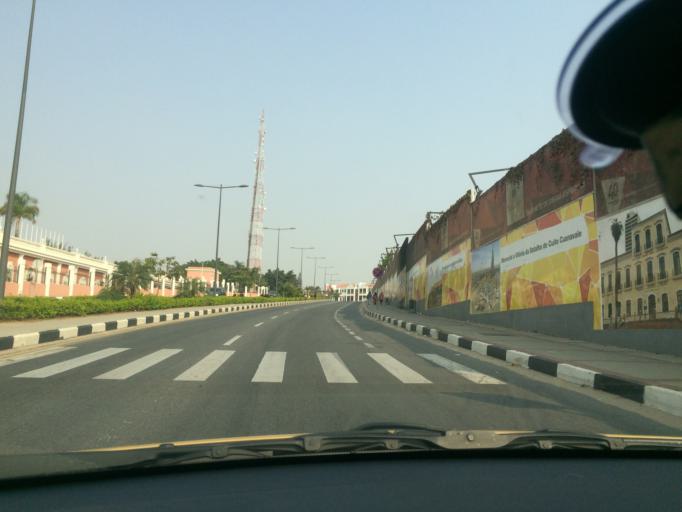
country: AO
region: Luanda
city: Luanda
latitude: -8.8226
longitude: 13.2230
